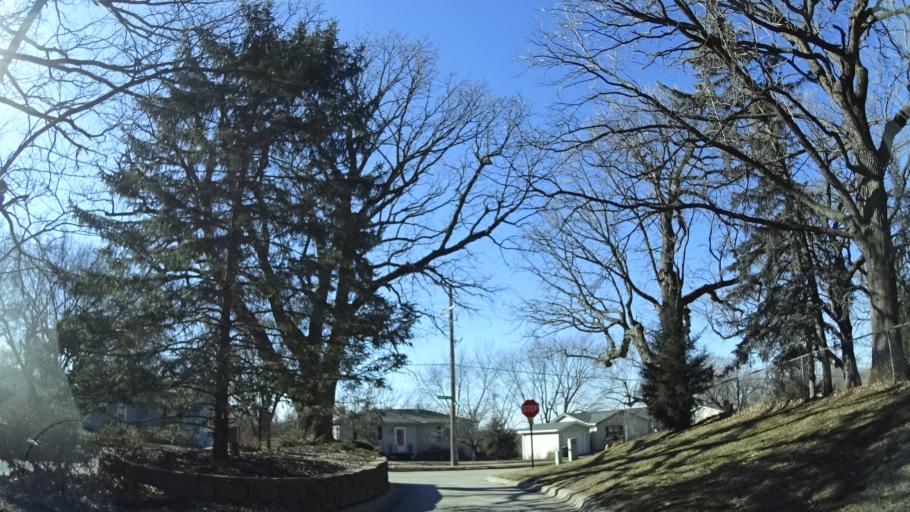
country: US
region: Nebraska
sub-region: Sarpy County
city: Bellevue
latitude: 41.1535
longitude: -95.8994
